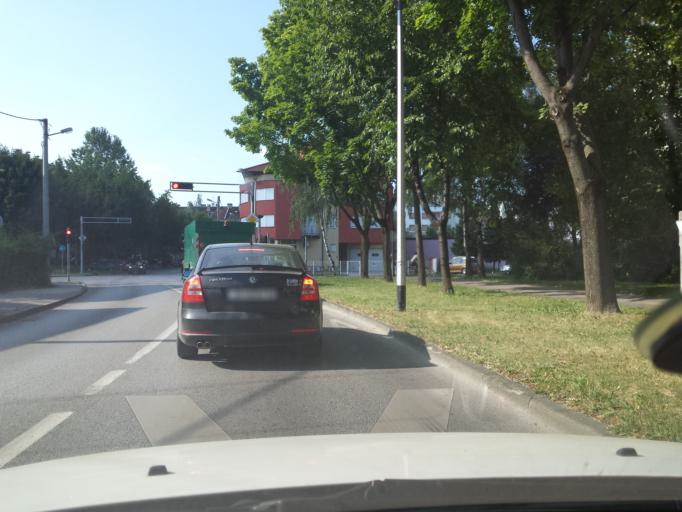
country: HR
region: Grad Zagreb
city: Jankomir
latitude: 45.8049
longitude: 15.9023
